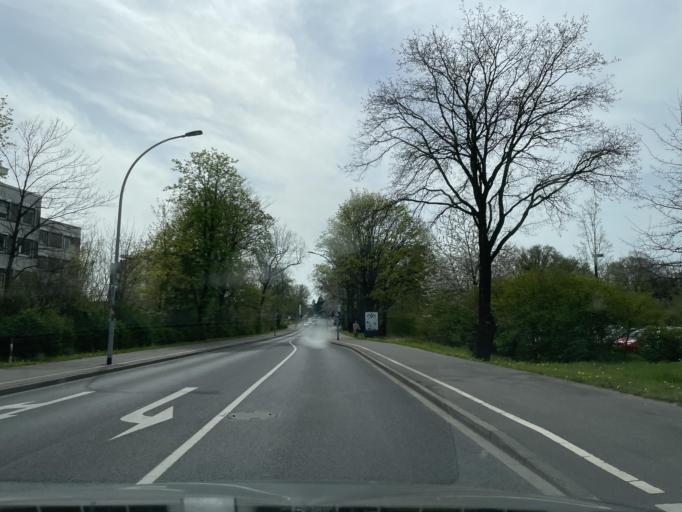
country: DE
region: North Rhine-Westphalia
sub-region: Regierungsbezirk Dusseldorf
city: Viersen
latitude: 51.2199
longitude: 6.4175
